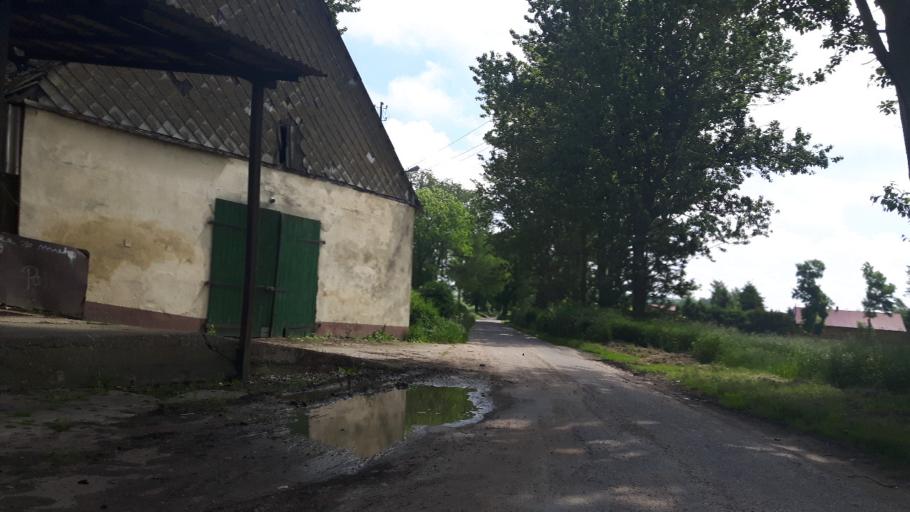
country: PL
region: West Pomeranian Voivodeship
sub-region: Powiat slawienski
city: Darlowo
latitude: 54.4711
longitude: 16.4700
